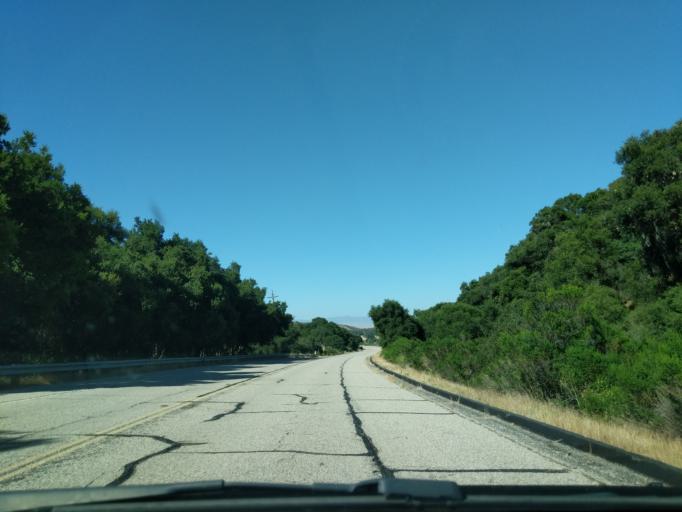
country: US
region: California
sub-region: Monterey County
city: King City
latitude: 36.0909
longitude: -121.1696
